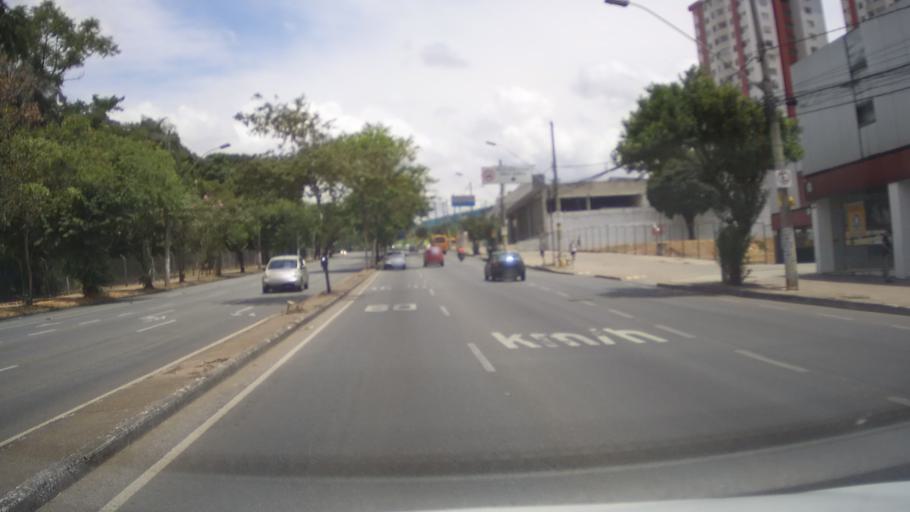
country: BR
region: Minas Gerais
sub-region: Belo Horizonte
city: Belo Horizonte
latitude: -19.8714
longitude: -43.9766
